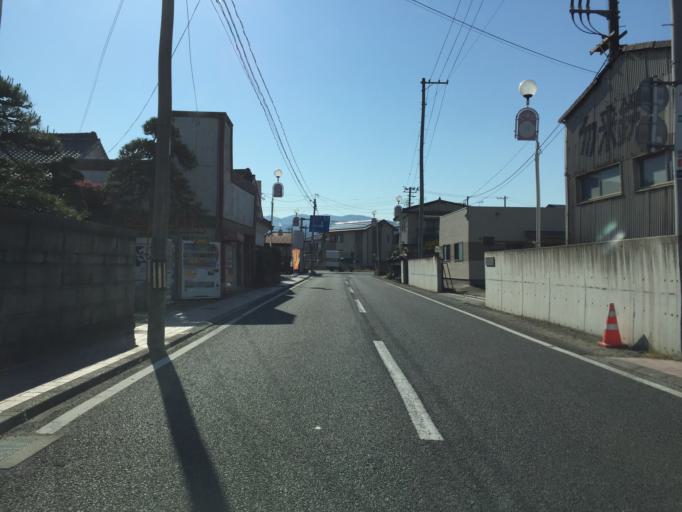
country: JP
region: Ibaraki
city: Kitaibaraki
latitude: 36.8914
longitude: 140.7616
